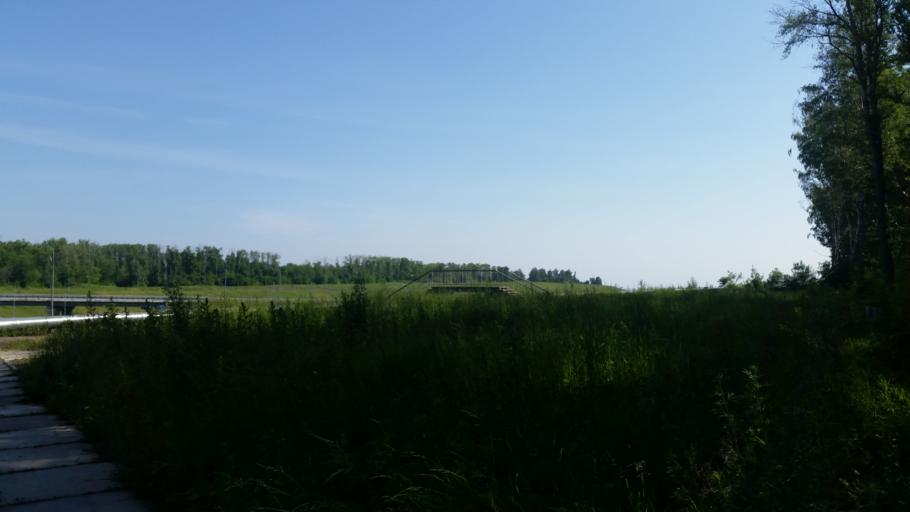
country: RU
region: Ulyanovsk
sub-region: Ulyanovskiy Rayon
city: Ulyanovsk
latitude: 54.3607
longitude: 48.3769
